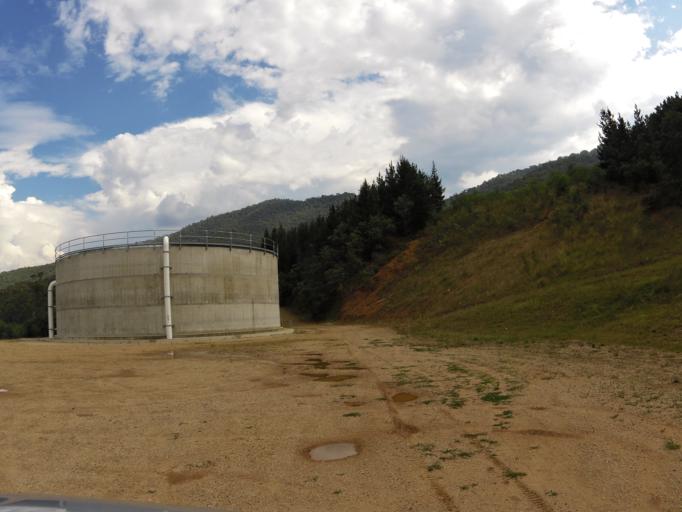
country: AU
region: Victoria
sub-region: Alpine
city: Mount Beauty
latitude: -36.7641
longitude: 147.0199
